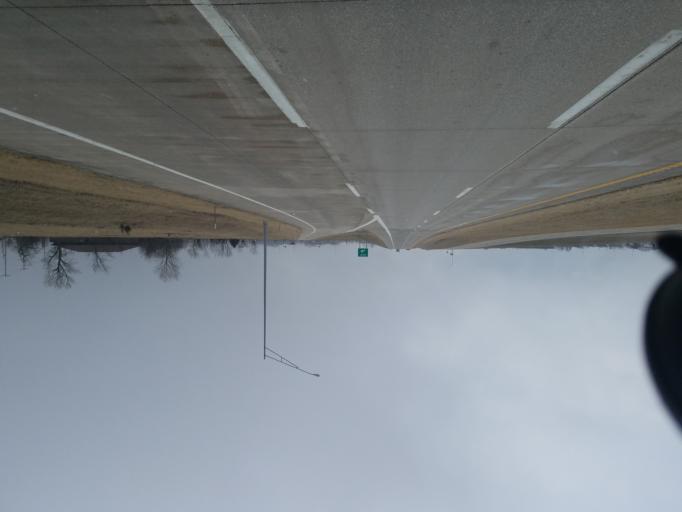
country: US
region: Missouri
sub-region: Randolph County
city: Moberly
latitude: 39.4480
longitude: -92.4273
